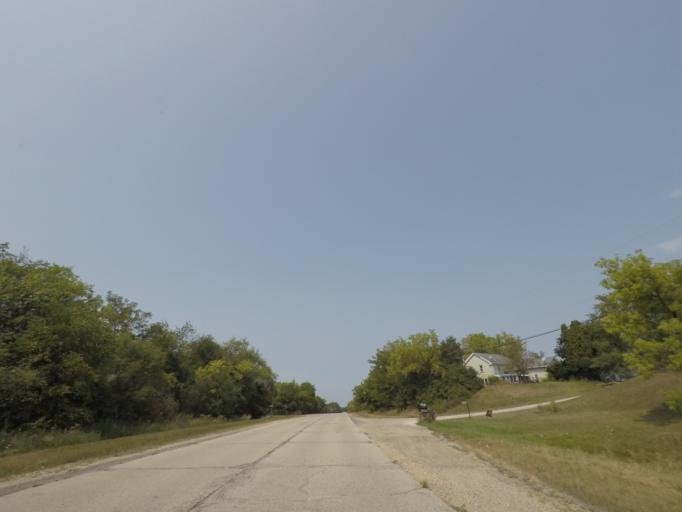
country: US
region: Wisconsin
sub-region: Waukesha County
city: Oconomowoc
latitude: 43.0624
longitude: -88.5377
